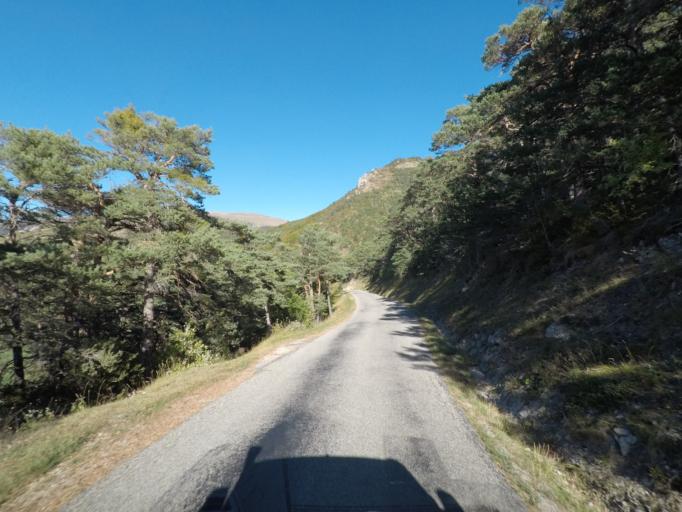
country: FR
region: Provence-Alpes-Cote d'Azur
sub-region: Departement des Hautes-Alpes
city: Serres
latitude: 44.4334
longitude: 5.5720
